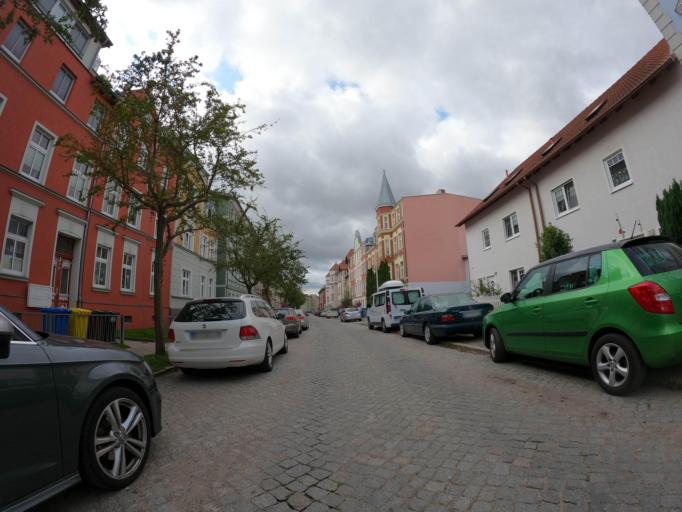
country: DE
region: Mecklenburg-Vorpommern
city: Stralsund
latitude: 54.3114
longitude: 13.0771
